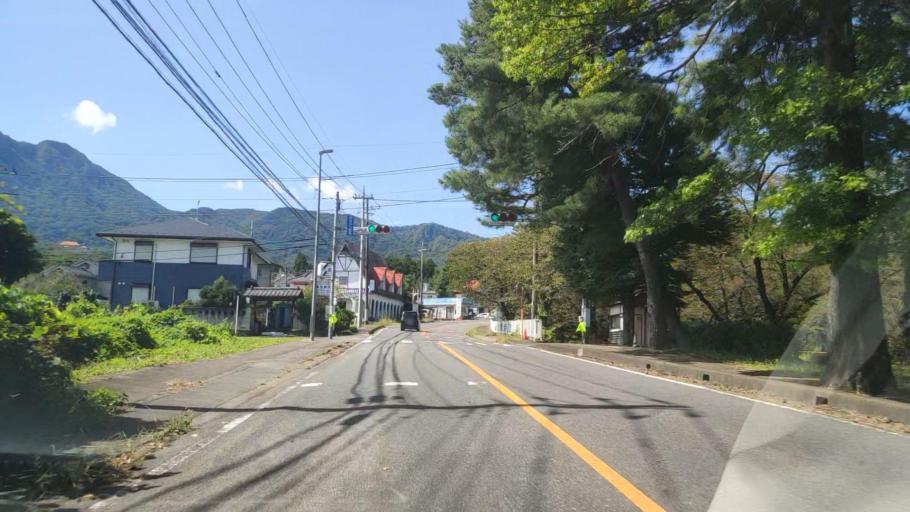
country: JP
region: Gunma
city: Shibukawa
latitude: 36.4982
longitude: 138.9534
